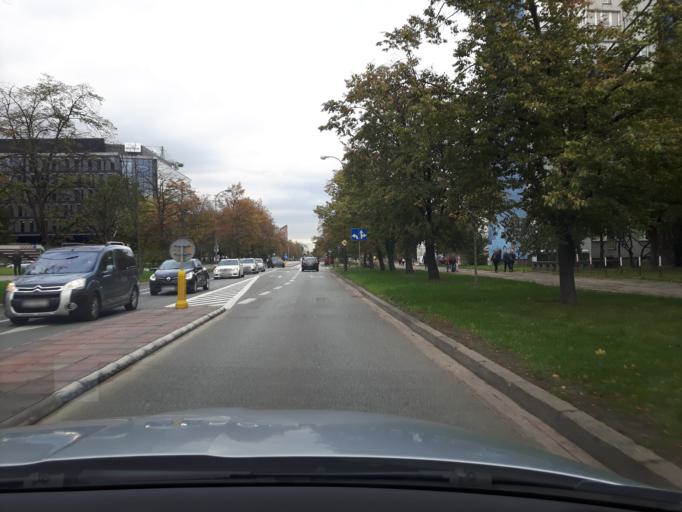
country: PL
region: Masovian Voivodeship
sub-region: Warszawa
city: Mokotow
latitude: 52.1834
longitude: 21.0106
